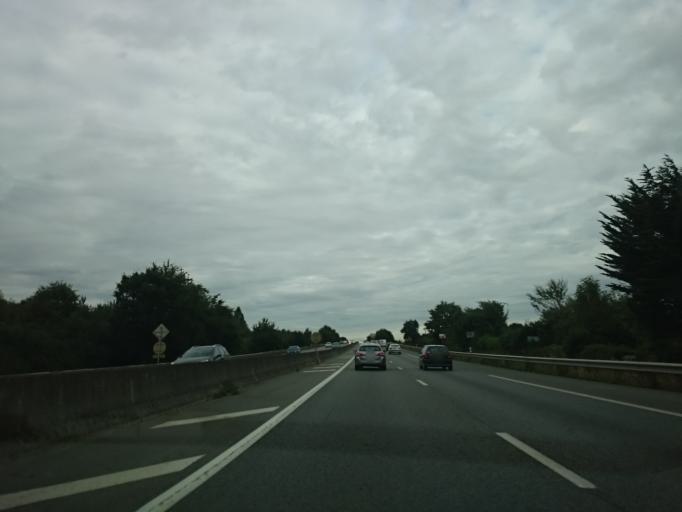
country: FR
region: Brittany
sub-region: Departement d'Ille-et-Vilaine
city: Chantepie
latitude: 48.0879
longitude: -1.6342
